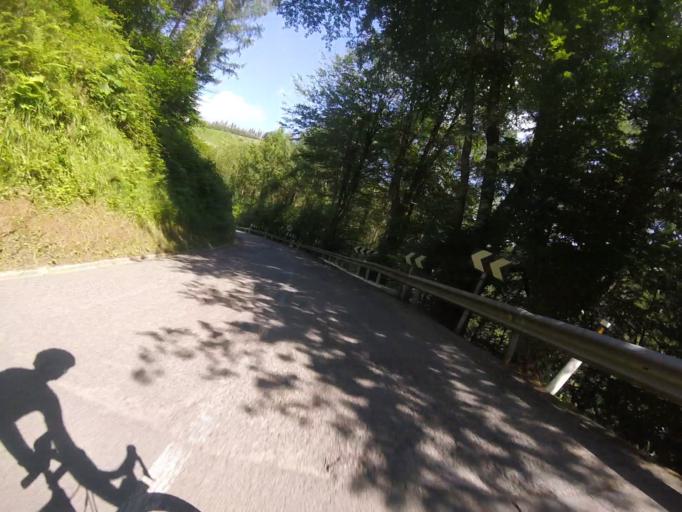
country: ES
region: Basque Country
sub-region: Provincia de Guipuzcoa
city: Ormaiztegui
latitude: 43.0979
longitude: -2.2438
